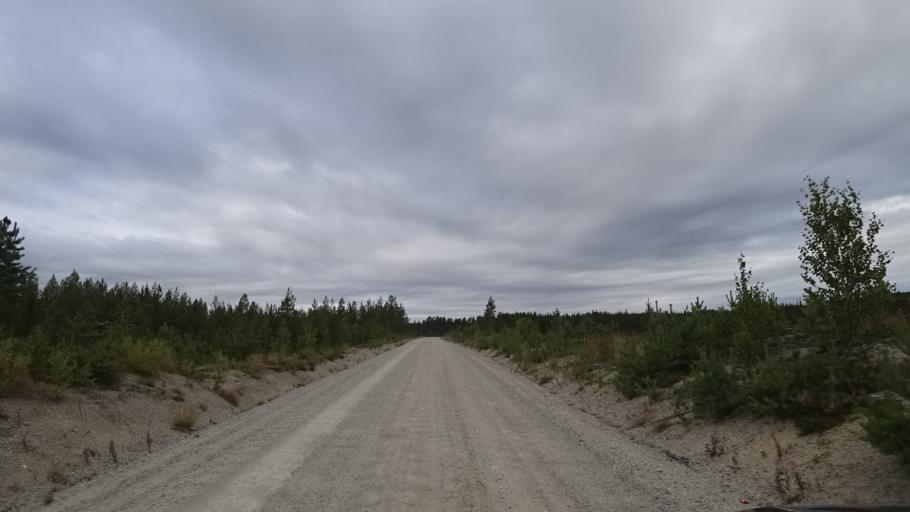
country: FI
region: North Karelia
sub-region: Pielisen Karjala
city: Lieksa
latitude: 63.2515
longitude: 30.3295
